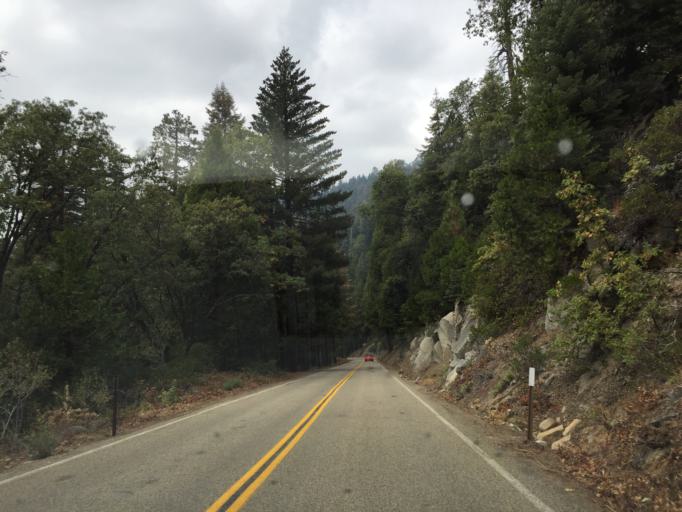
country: US
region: California
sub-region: Tulare County
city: Three Rivers
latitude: 36.7170
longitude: -118.9269
